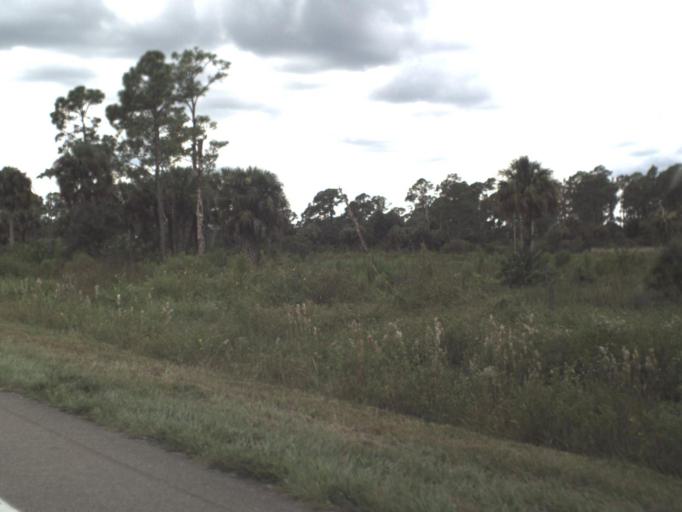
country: US
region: Florida
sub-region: Lee County
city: Olga
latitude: 26.8548
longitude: -81.7597
